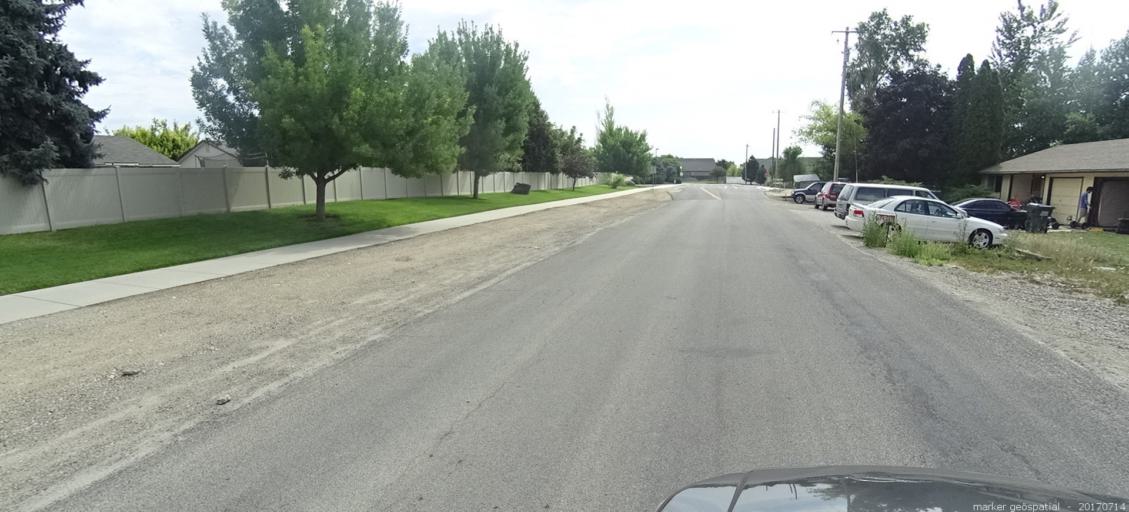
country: US
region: Idaho
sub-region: Ada County
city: Kuna
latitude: 43.4920
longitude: -116.4056
